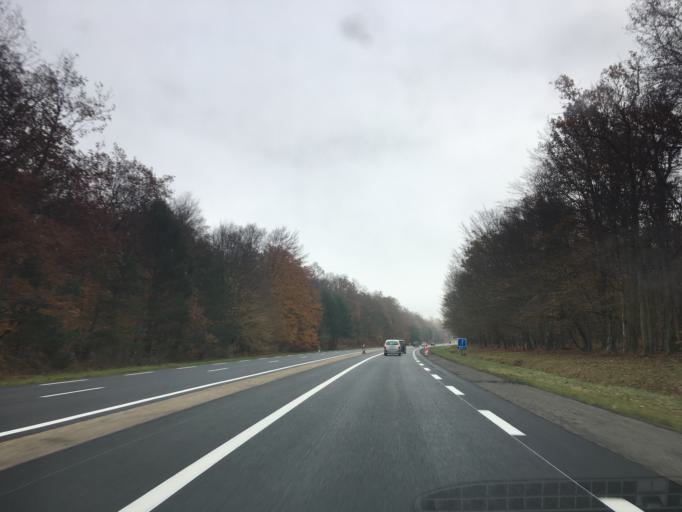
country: FR
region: Ile-de-France
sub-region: Departement de Seine-et-Marne
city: Avon
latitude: 48.3946
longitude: 2.7446
